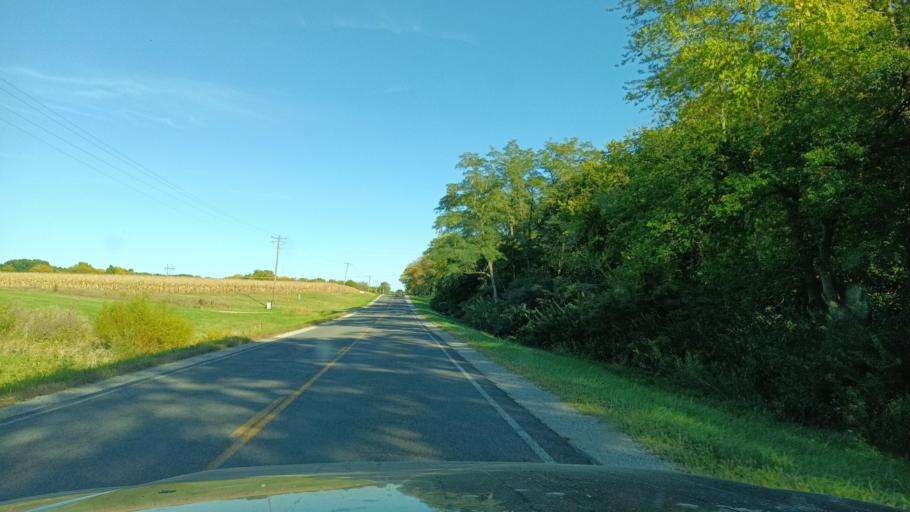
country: US
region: Illinois
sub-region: McLean County
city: Le Roy
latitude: 40.2245
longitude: -88.8336
